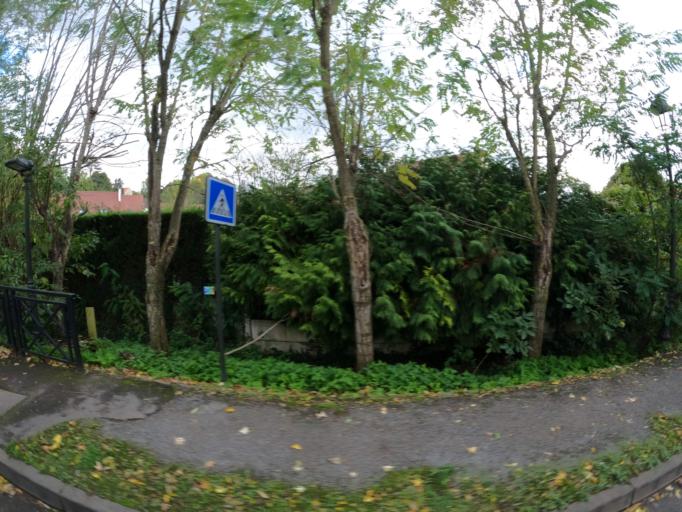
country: FR
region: Ile-de-France
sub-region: Departement de Seine-et-Marne
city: Coupvray
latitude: 48.8955
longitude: 2.7940
